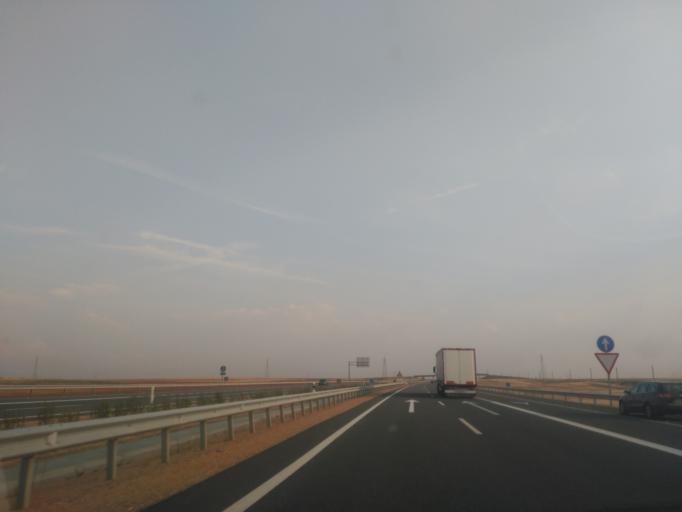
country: ES
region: Castille and Leon
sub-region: Provincia de Zamora
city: Montamarta
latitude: 41.6304
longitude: -5.7890
